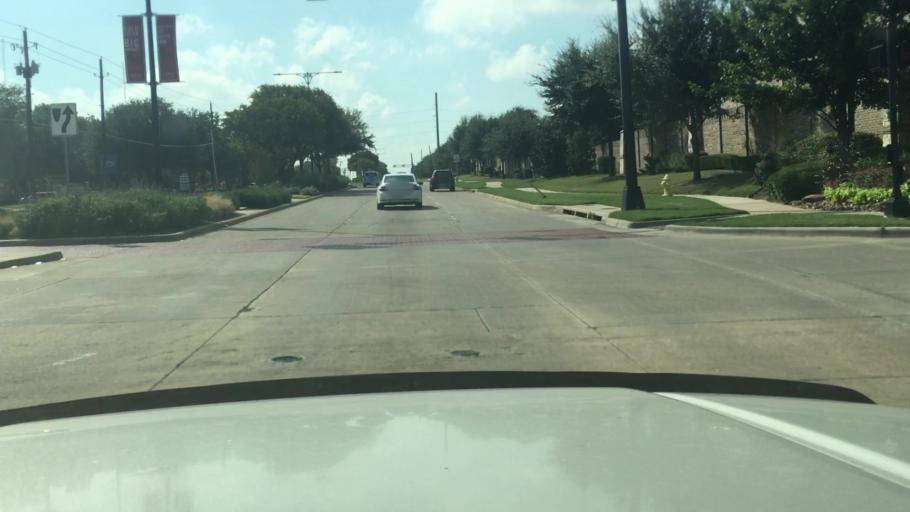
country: US
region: Texas
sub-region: Dallas County
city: Coppell
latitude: 32.9544
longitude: -96.9936
